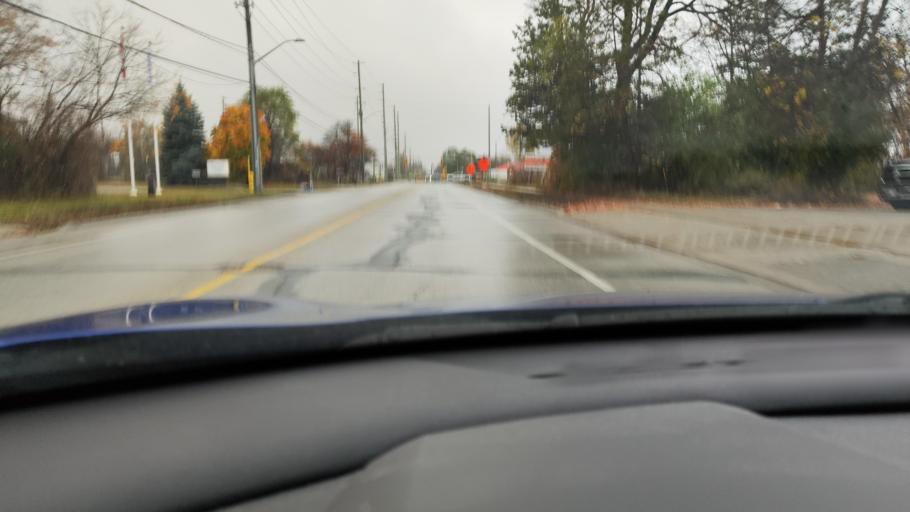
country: CA
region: Ontario
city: Barrie
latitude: 44.3736
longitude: -79.6952
